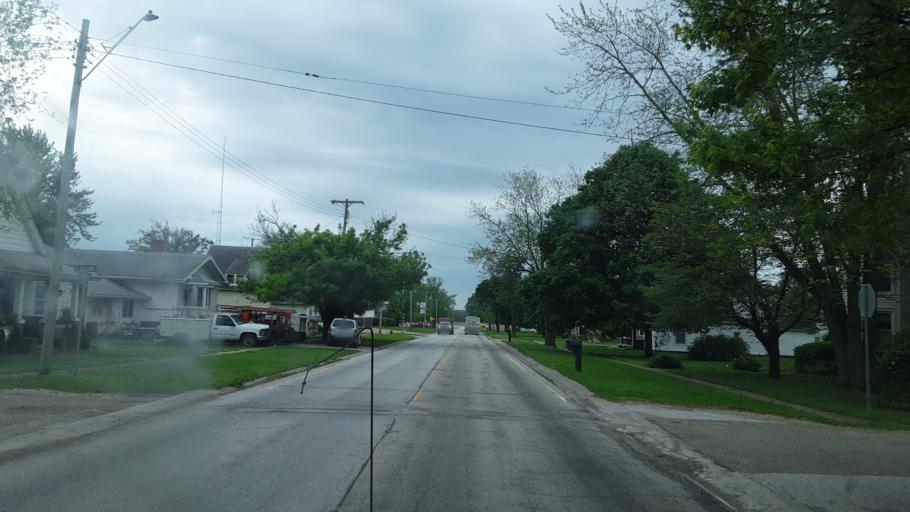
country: US
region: Illinois
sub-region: Fulton County
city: Astoria
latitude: 40.3630
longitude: -90.4253
